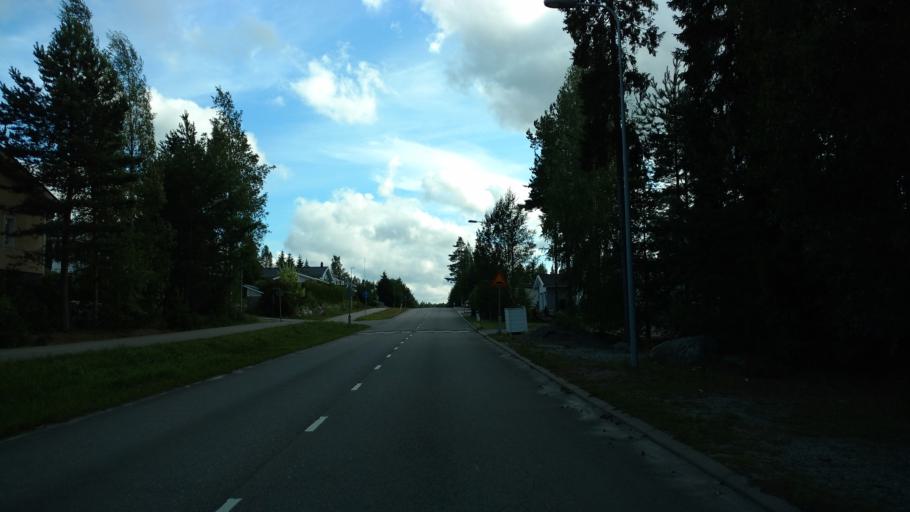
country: FI
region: Varsinais-Suomi
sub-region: Salo
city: Salo
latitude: 60.4040
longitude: 23.1818
